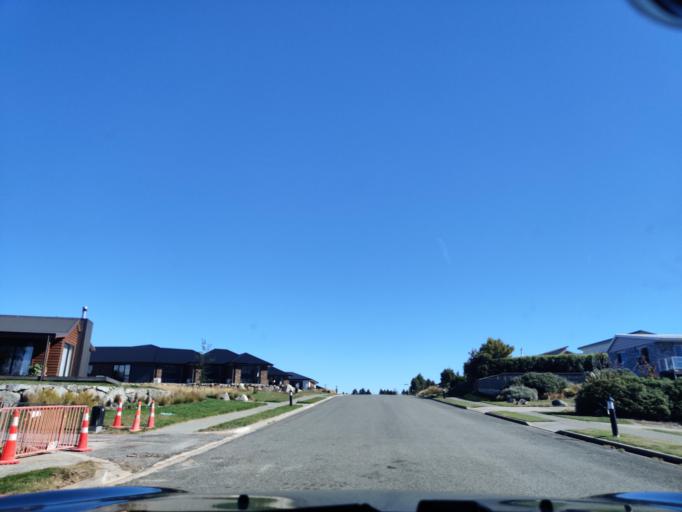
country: NZ
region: Canterbury
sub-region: Timaru District
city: Pleasant Point
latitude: -44.0071
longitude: 170.4748
